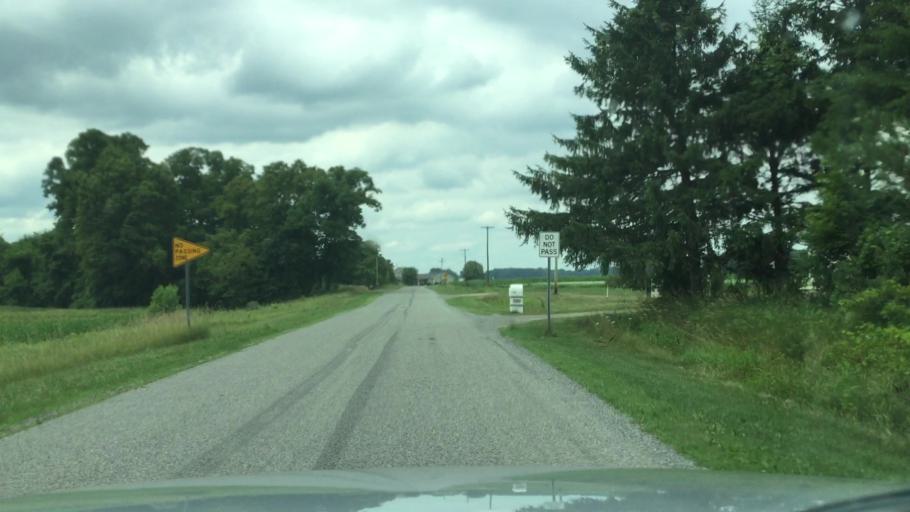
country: US
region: Michigan
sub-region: Saginaw County
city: Burt
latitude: 43.2603
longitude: -83.8776
